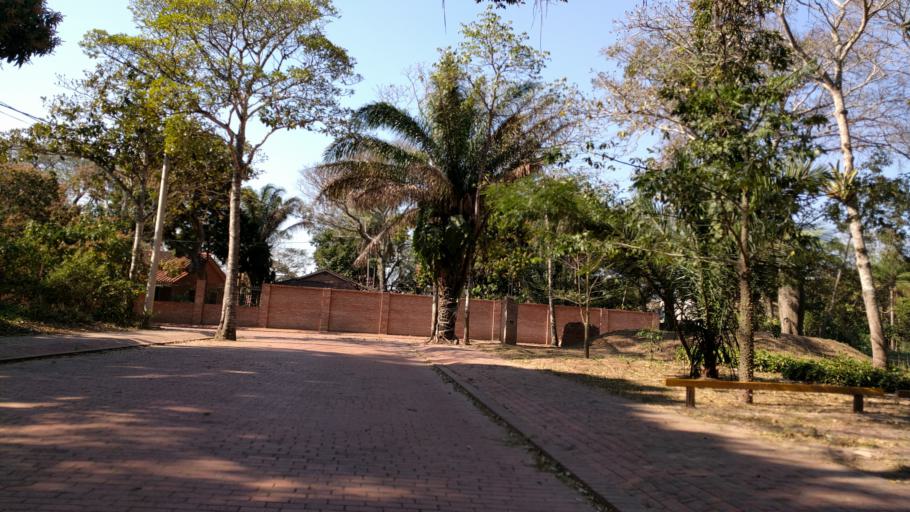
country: BO
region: Santa Cruz
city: Santa Cruz de la Sierra
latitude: -17.8080
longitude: -63.2241
